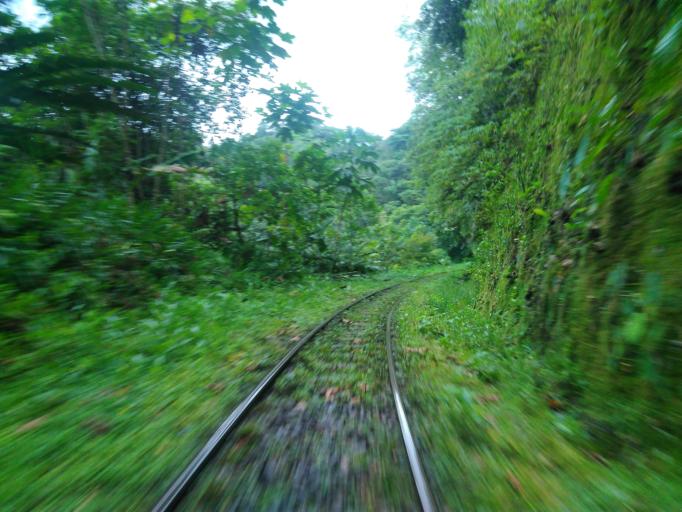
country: CO
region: Valle del Cauca
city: Buenaventura
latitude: 3.8408
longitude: -76.8737
